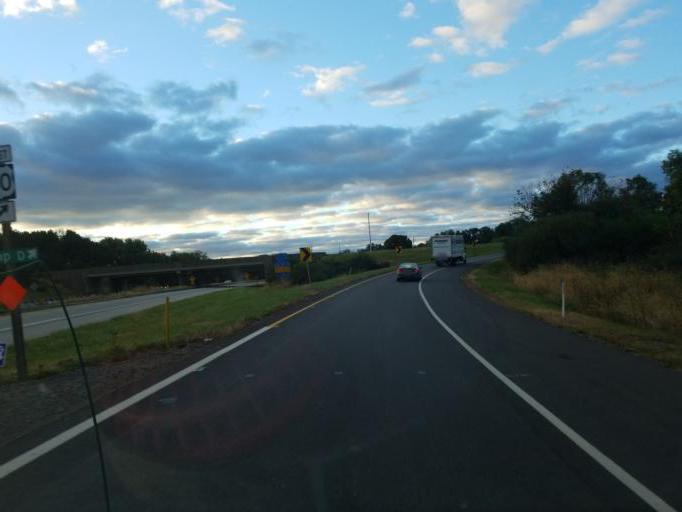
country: US
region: Pennsylvania
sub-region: York County
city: Shiloh
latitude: 39.9384
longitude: -76.7998
